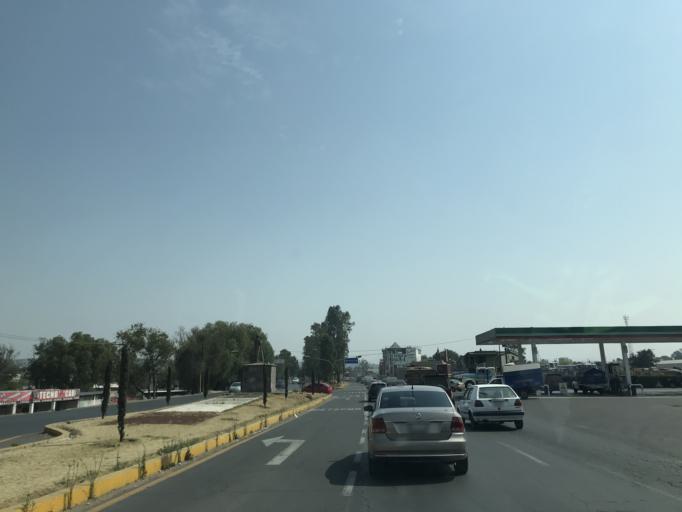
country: MX
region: Tlaxcala
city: Tlaxcala de Xicohtencatl
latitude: 19.3197
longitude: -98.2021
